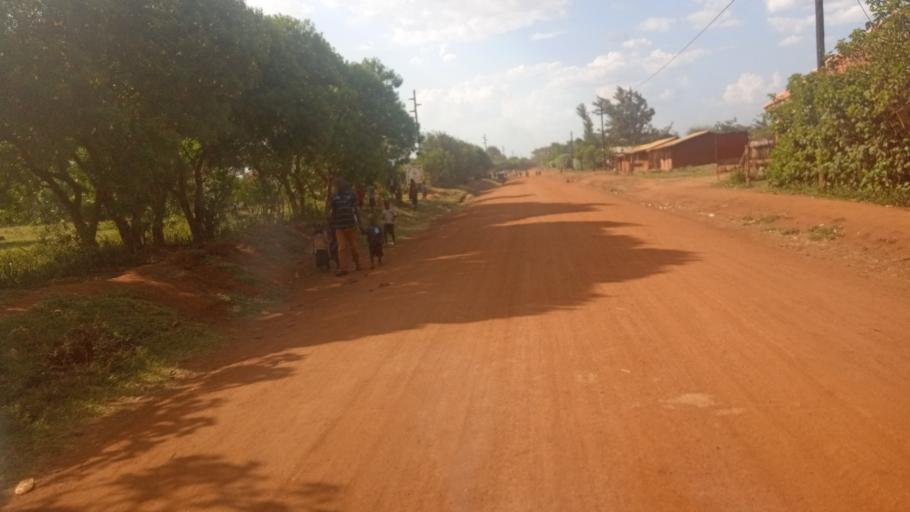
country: UG
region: Eastern Region
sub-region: Kween District
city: Binyin
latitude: 1.5059
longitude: 34.5000
